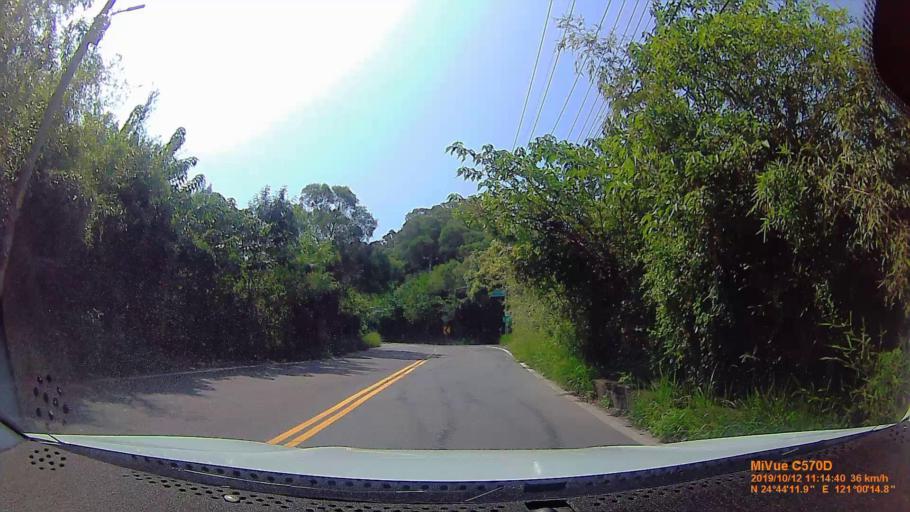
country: TW
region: Taiwan
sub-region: Hsinchu
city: Hsinchu
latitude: 24.7366
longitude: 121.0041
